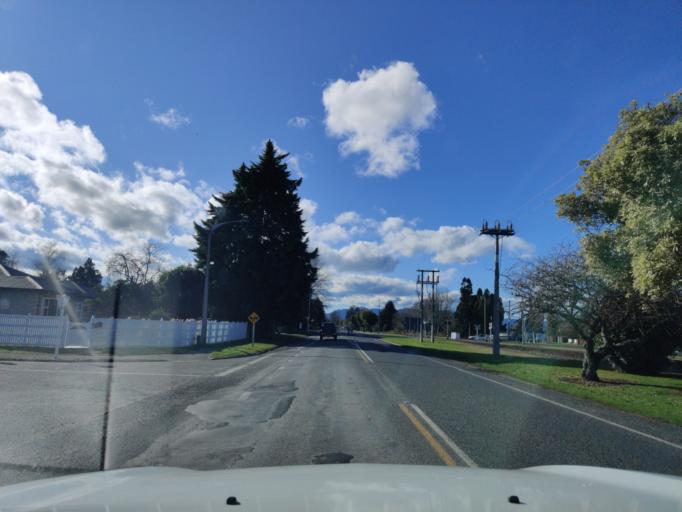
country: NZ
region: Waikato
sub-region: Matamata-Piako District
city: Matamata
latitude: -37.8263
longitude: 175.7695
